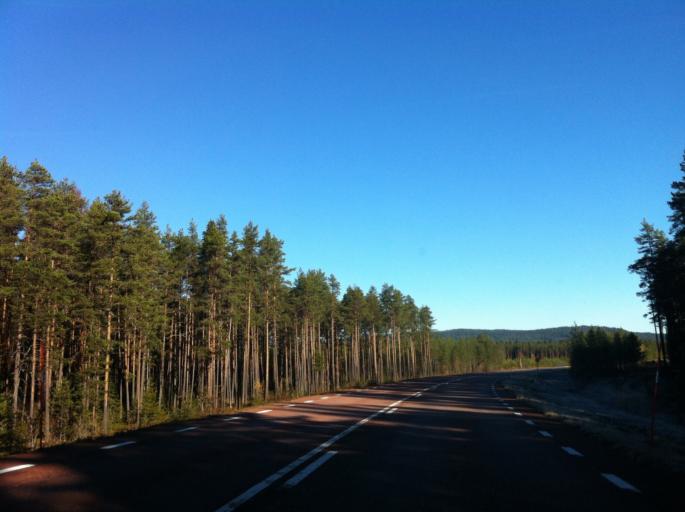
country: SE
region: Dalarna
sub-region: Alvdalens Kommun
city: AElvdalen
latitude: 61.2748
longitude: 13.8397
